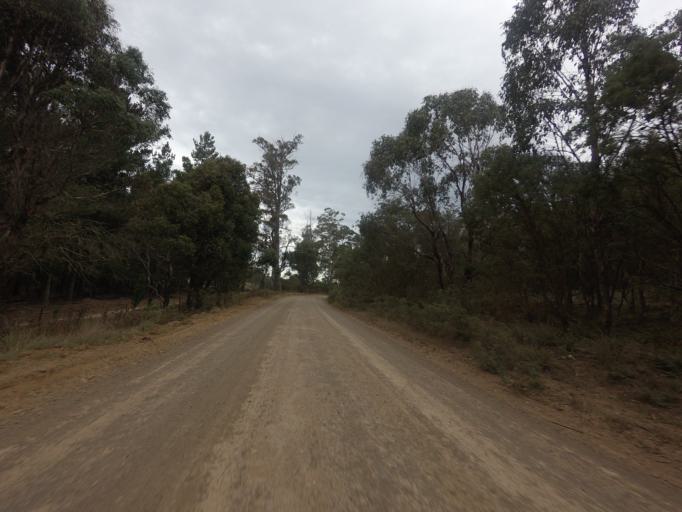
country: AU
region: Tasmania
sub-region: Derwent Valley
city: New Norfolk
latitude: -42.5754
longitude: 147.0003
